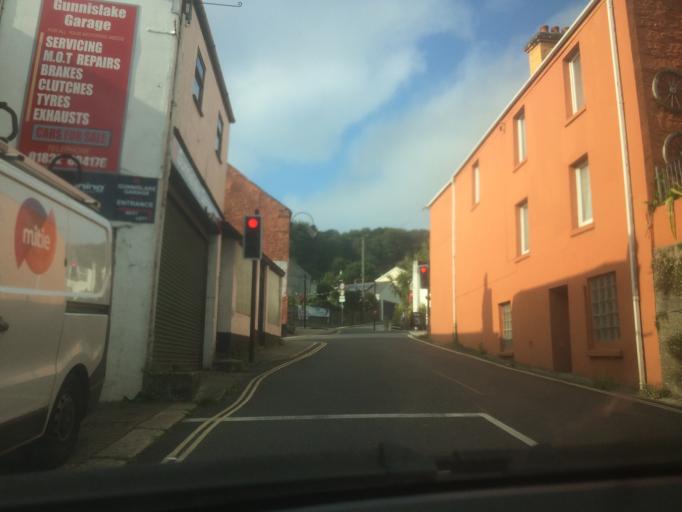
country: GB
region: England
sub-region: Cornwall
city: Gunnislake
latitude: 50.5247
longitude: -4.2131
